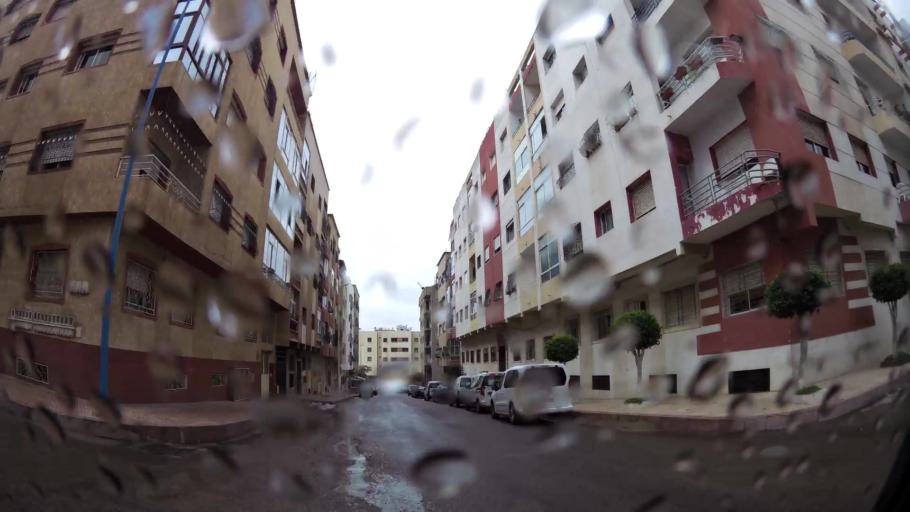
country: MA
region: Grand Casablanca
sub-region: Mediouna
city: Tit Mellil
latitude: 33.6220
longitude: -7.4856
